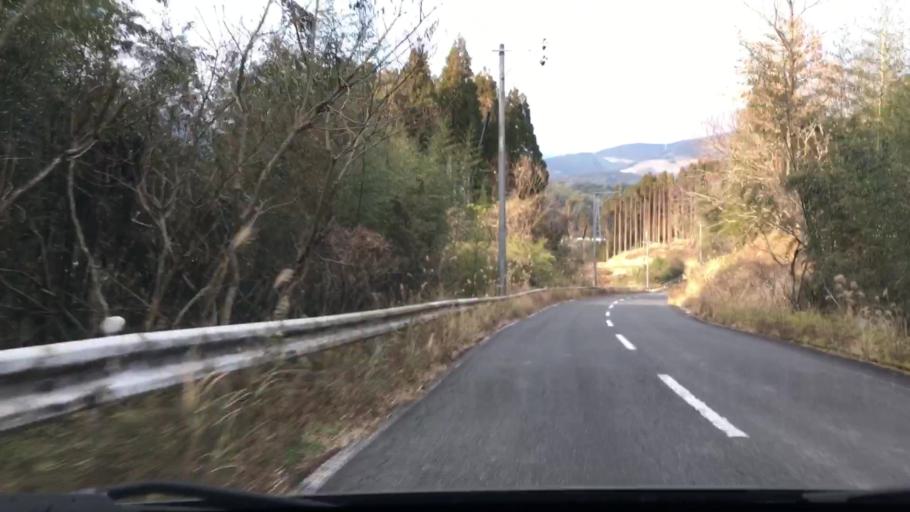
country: JP
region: Miyazaki
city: Nichinan
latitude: 31.6078
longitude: 131.3297
